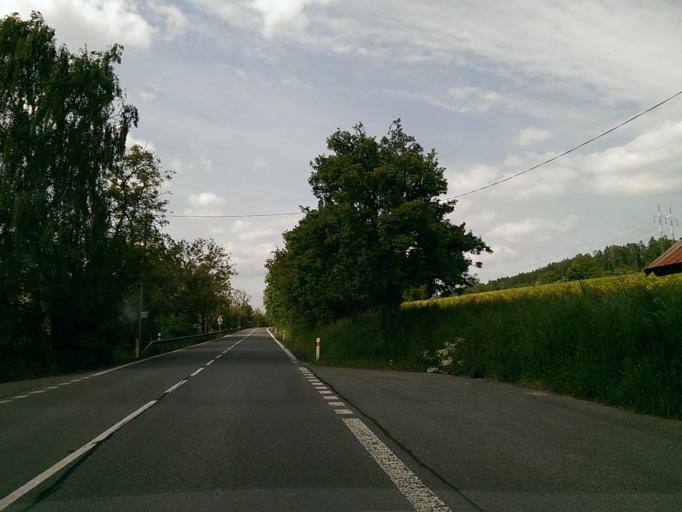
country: CZ
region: Liberecky
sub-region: Okres Semily
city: Turnov
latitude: 50.6088
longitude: 15.1648
